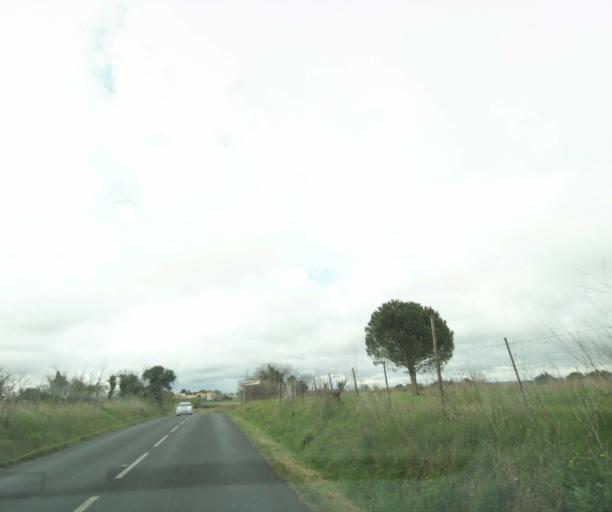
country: FR
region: Languedoc-Roussillon
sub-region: Departement de l'Herault
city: Fabregues
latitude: 43.5602
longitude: 3.7756
